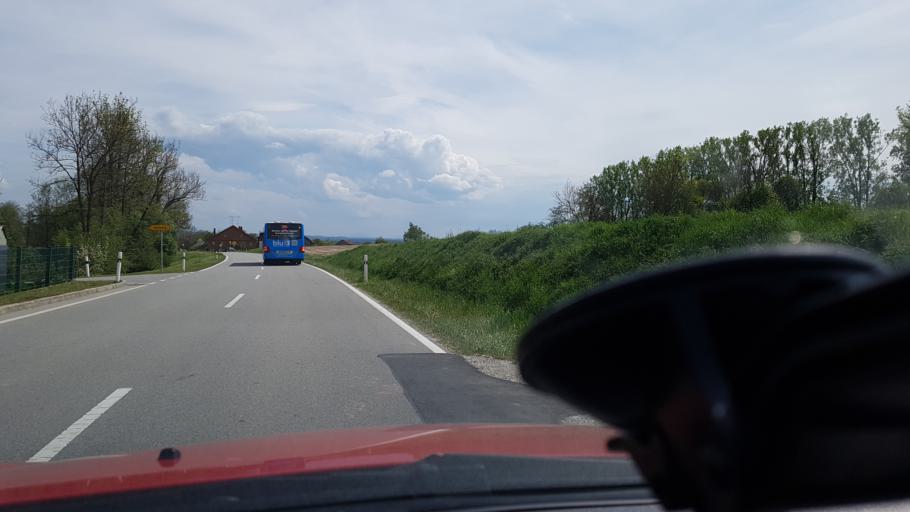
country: DE
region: Bavaria
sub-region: Lower Bavaria
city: Ering
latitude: 48.3132
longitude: 13.1374
